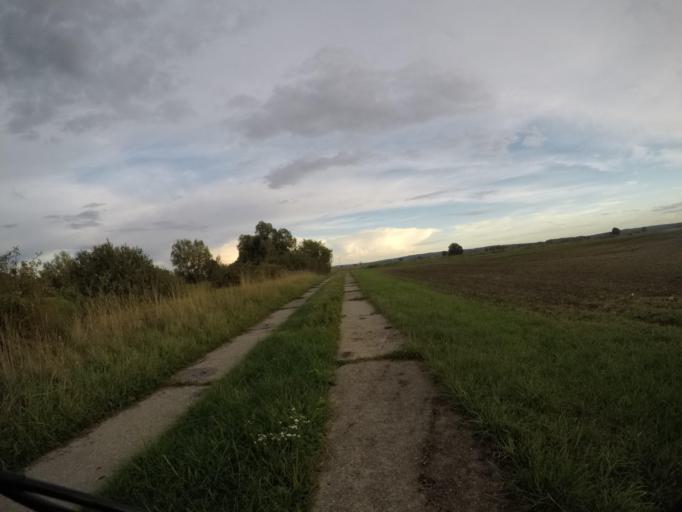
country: DE
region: Lower Saxony
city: Neu Darchau
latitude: 53.2674
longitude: 10.8964
